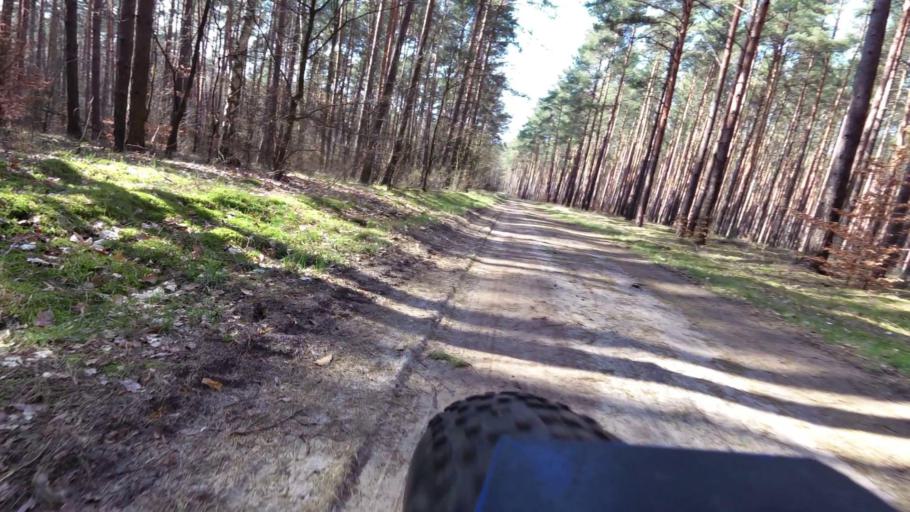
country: PL
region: Lubusz
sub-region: Powiat slubicki
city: Cybinka
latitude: 52.2311
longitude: 14.8299
